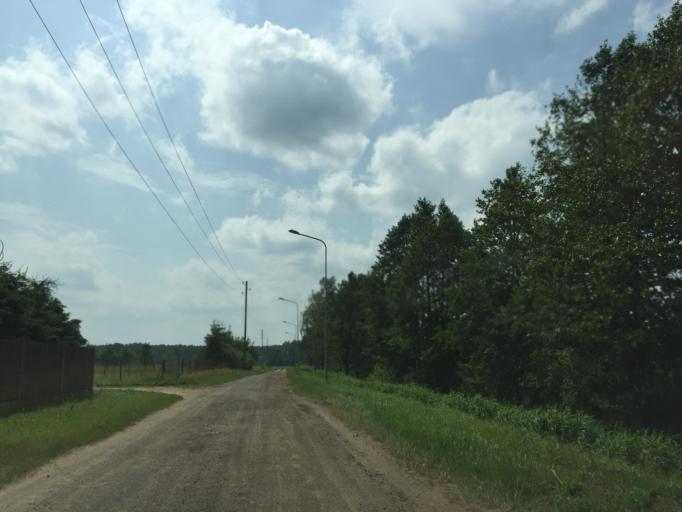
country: LV
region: Olaine
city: Olaine
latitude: 56.7764
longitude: 23.9191
